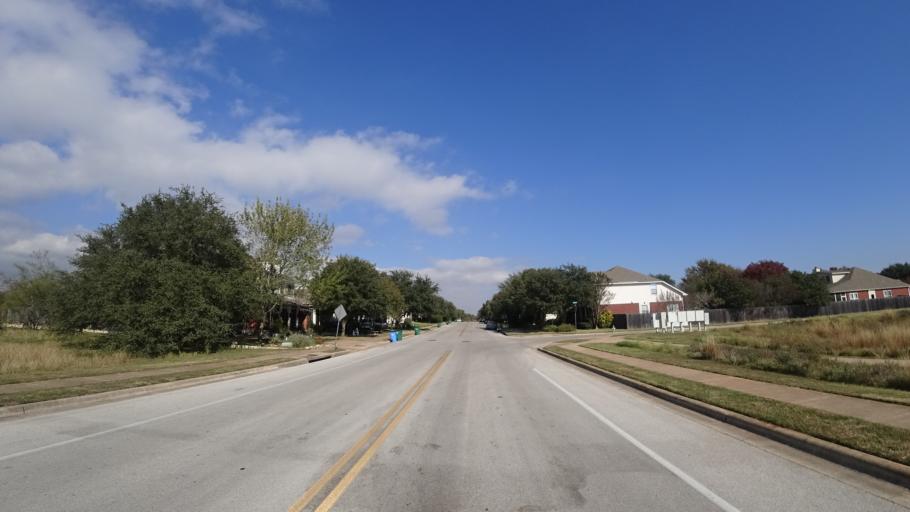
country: US
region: Texas
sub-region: Travis County
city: Shady Hollow
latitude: 30.1696
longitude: -97.8740
